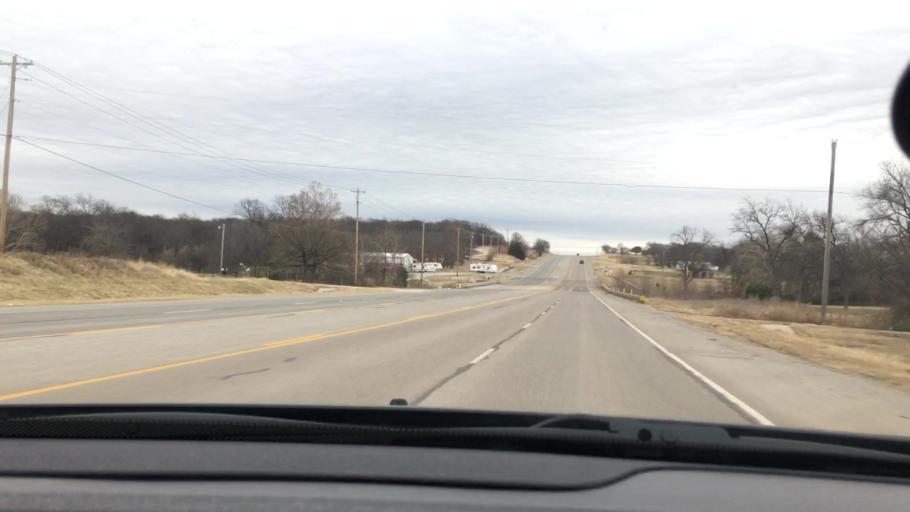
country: US
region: Oklahoma
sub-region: Carter County
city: Dickson
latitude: 34.1871
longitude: -97.0323
